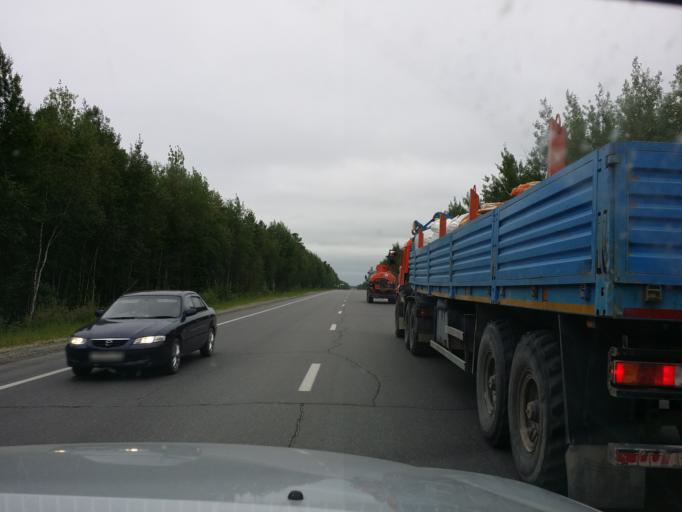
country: RU
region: Khanty-Mansiyskiy Avtonomnyy Okrug
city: Megion
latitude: 61.0560
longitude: 76.3031
